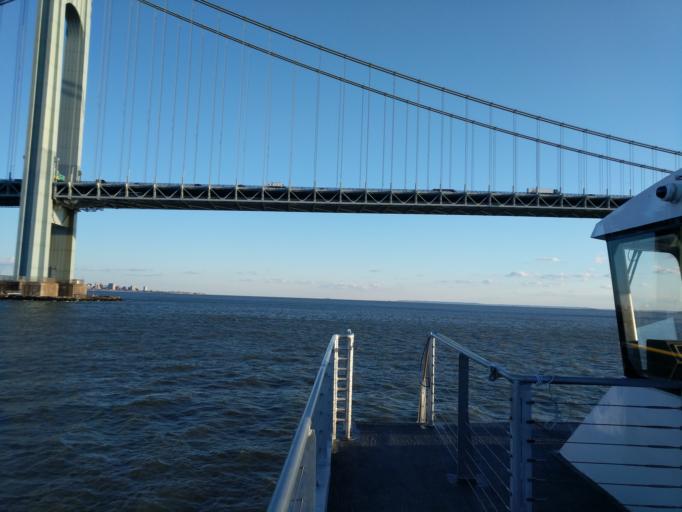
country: US
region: New York
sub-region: Kings County
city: Bensonhurst
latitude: 40.6106
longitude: -74.0413
